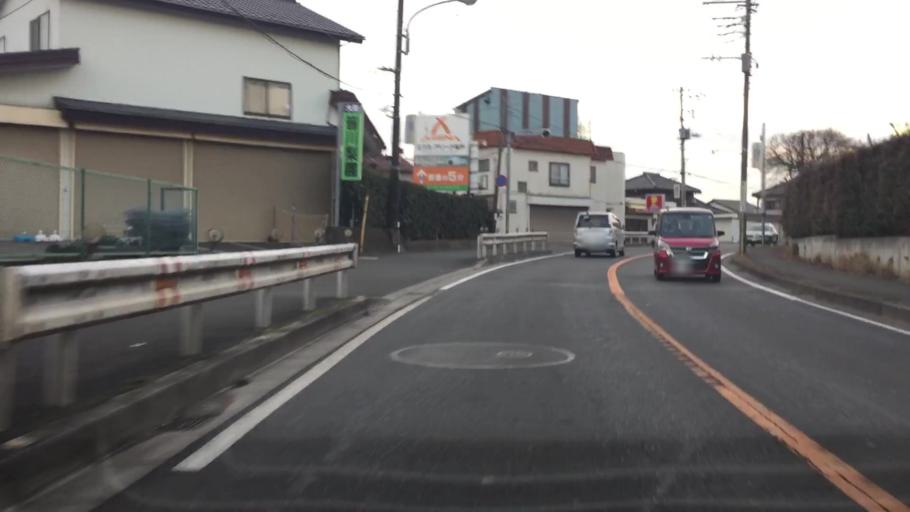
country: JP
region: Chiba
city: Matsudo
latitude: 35.7750
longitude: 139.9728
